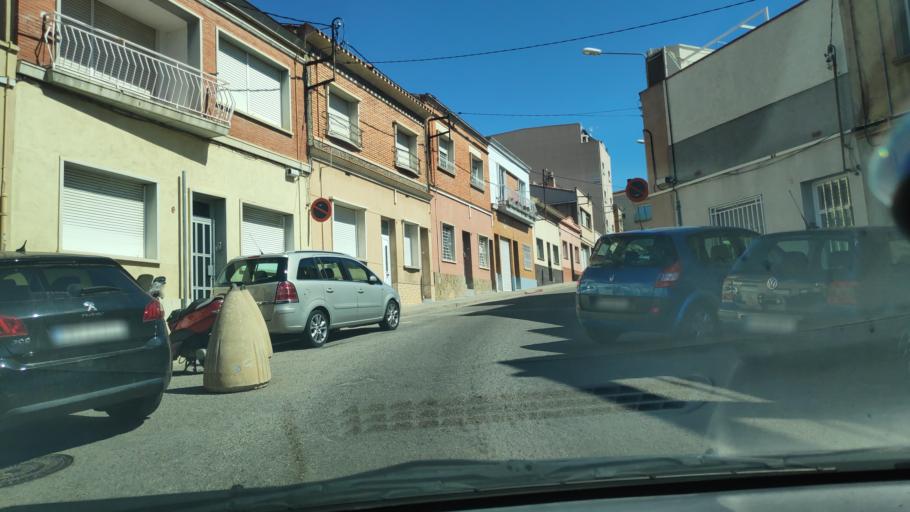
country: ES
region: Catalonia
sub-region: Provincia de Barcelona
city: Sant Quirze del Valles
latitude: 41.5477
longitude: 2.0912
